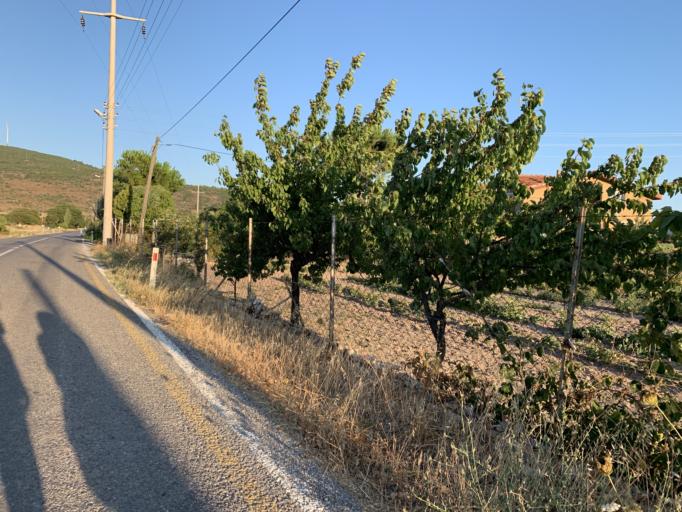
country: TR
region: Izmir
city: Uzunkuyu
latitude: 38.3236
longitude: 26.5715
